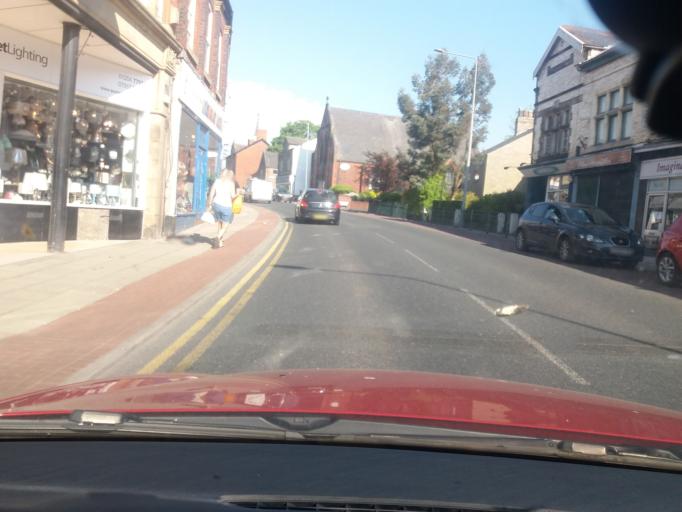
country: GB
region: England
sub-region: Borough of Bolton
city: Horwich
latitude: 53.6007
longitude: -2.5471
